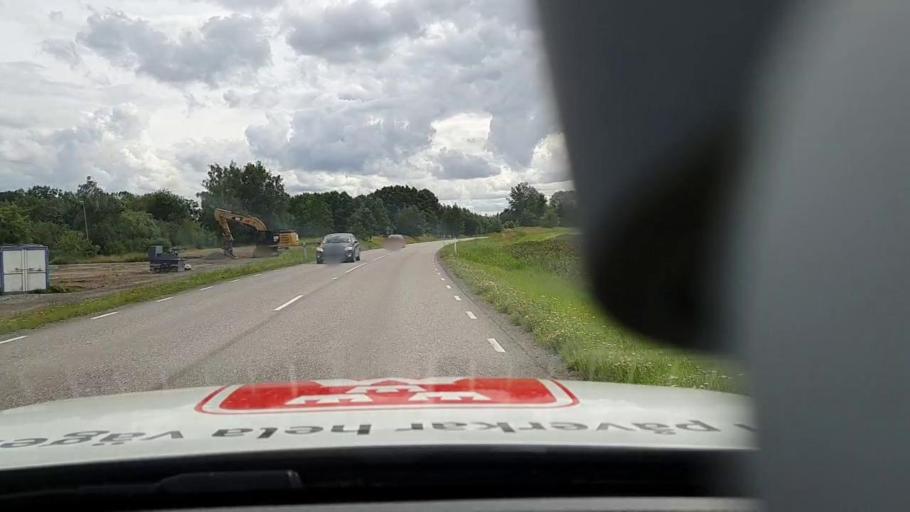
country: SE
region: Vaestra Goetaland
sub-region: Lidkopings Kommun
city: Lidkoping
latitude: 58.5415
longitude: 13.1133
